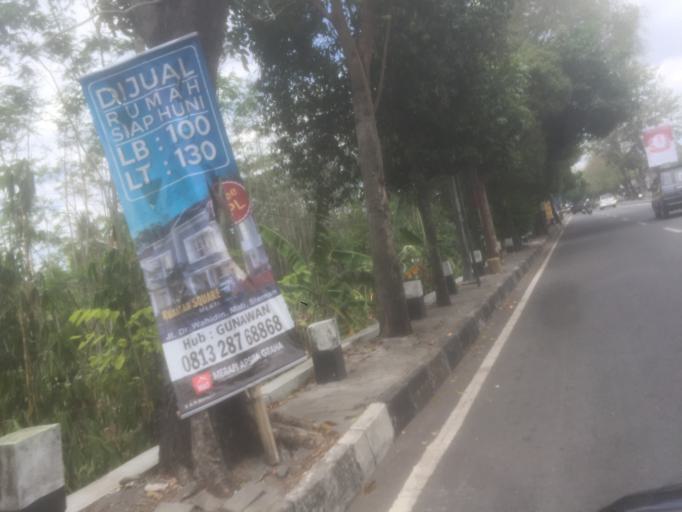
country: ID
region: Daerah Istimewa Yogyakarta
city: Melati
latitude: -7.7270
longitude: 110.3630
